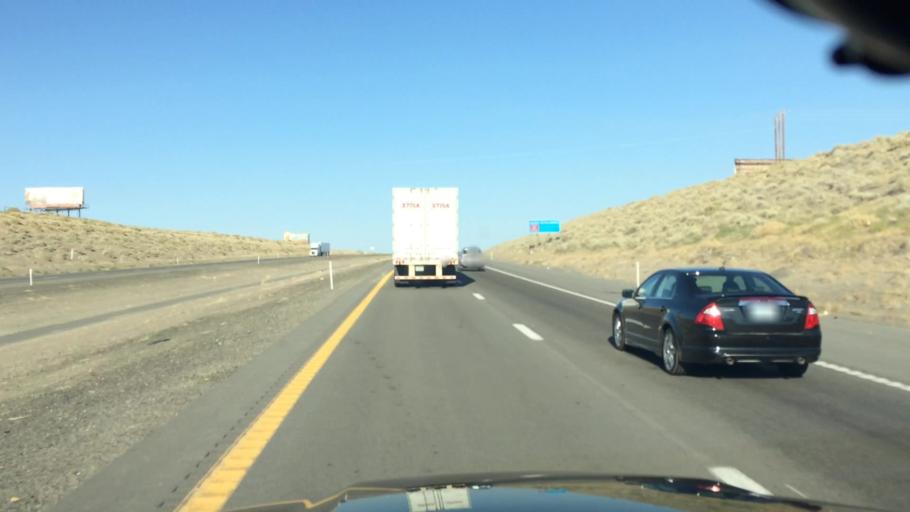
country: US
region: Nevada
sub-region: Lyon County
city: Fernley
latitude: 39.6182
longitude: -119.2850
